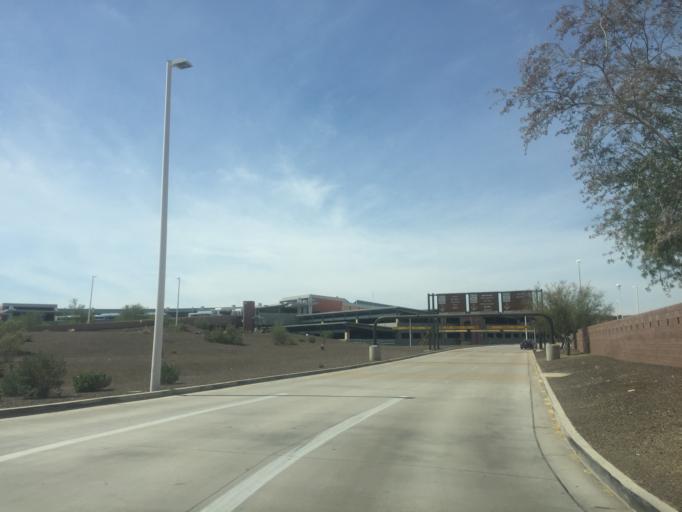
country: US
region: Arizona
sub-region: Maricopa County
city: Phoenix
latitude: 33.4330
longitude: -112.0436
